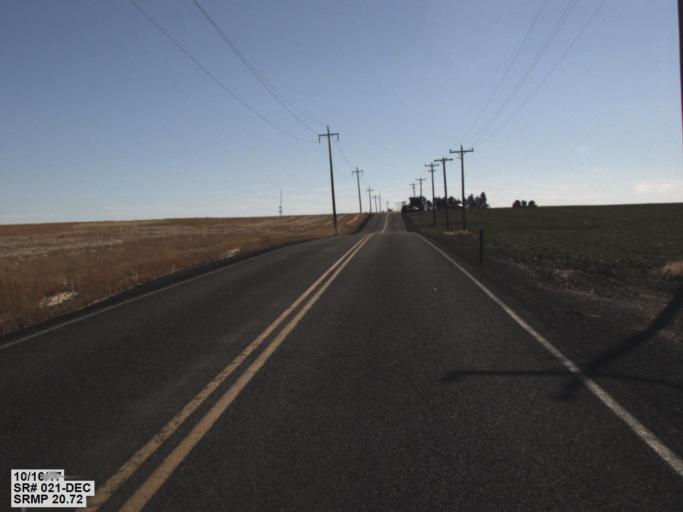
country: US
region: Washington
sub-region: Adams County
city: Ritzville
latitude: 46.9202
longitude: -118.5672
